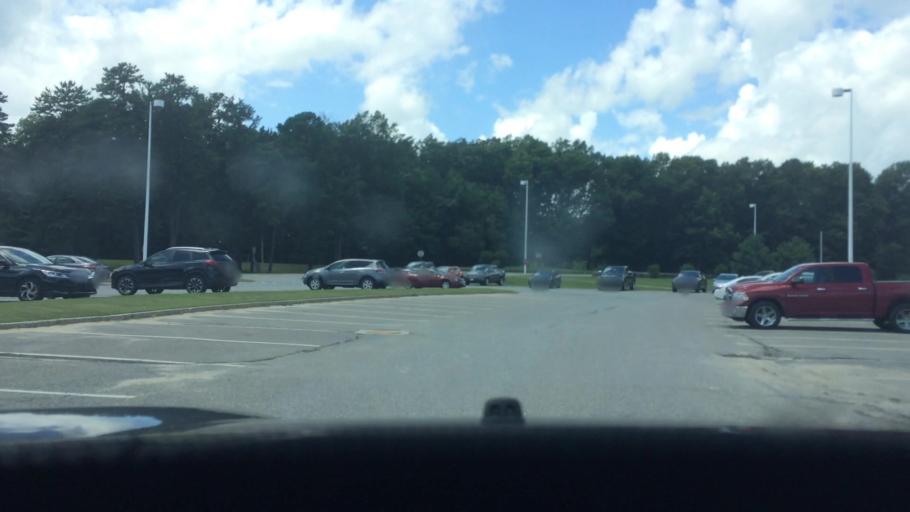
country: US
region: Massachusetts
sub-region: Middlesex County
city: Shirley
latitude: 42.5268
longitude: -71.6250
